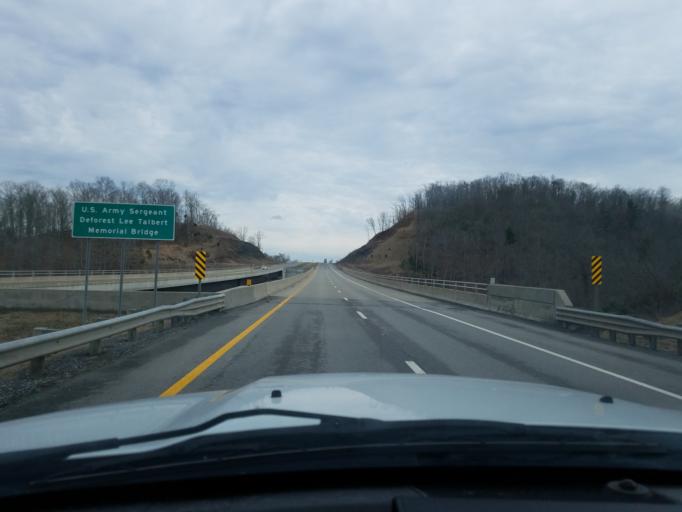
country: US
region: West Virginia
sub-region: Putnam County
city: Buffalo
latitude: 38.5560
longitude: -82.0022
